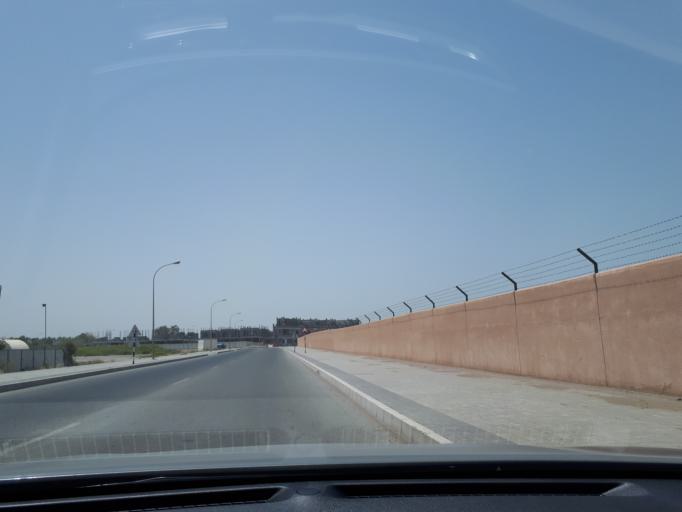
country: OM
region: Muhafazat Masqat
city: As Sib al Jadidah
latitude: 23.6822
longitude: 58.1435
